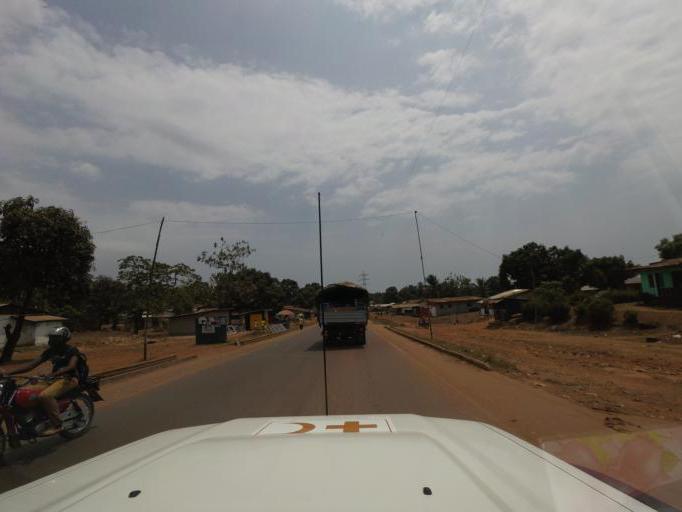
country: LR
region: Montserrado
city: Monrovia
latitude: 6.3041
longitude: -10.6907
